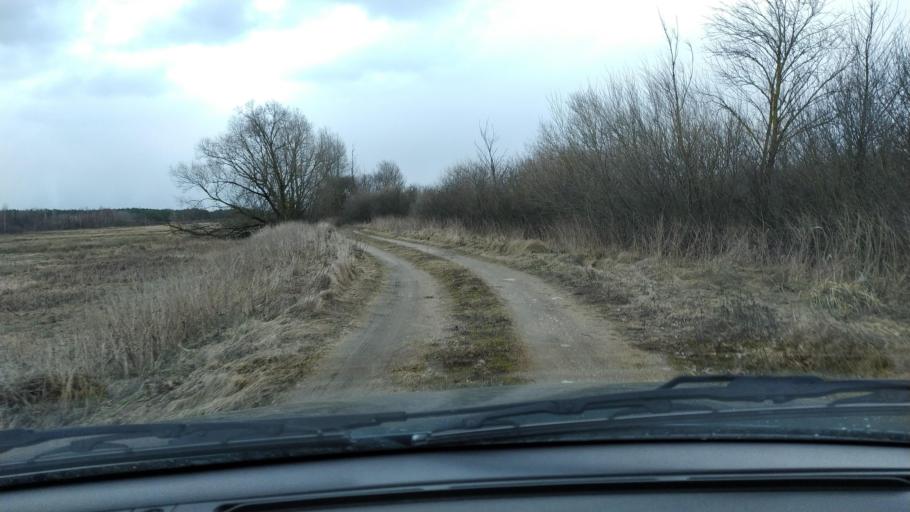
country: BY
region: Brest
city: Zhabinka
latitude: 52.4116
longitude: 24.0612
